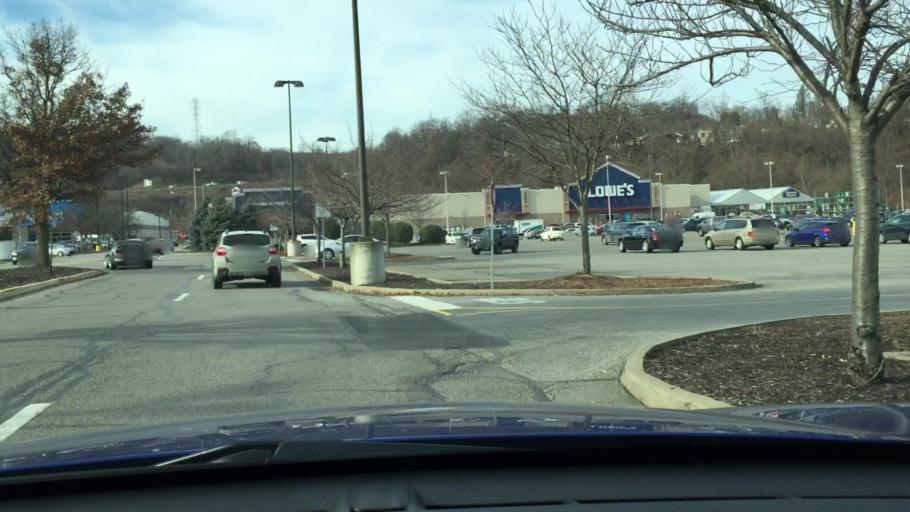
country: US
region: Pennsylvania
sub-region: Allegheny County
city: Heidelberg
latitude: 40.3867
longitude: -80.0928
